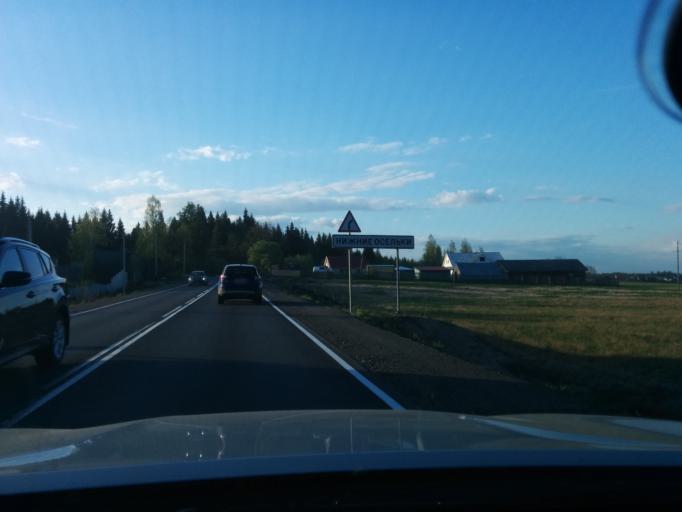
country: RU
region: Leningrad
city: Verkhniye Osel'ki
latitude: 60.2126
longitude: 30.4267
